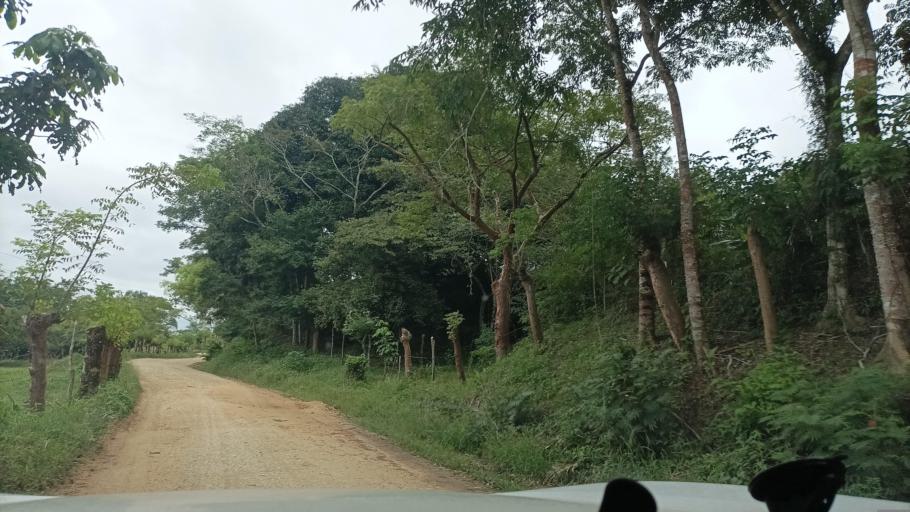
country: MX
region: Veracruz
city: Hidalgotitlan
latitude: 17.6346
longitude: -94.5115
